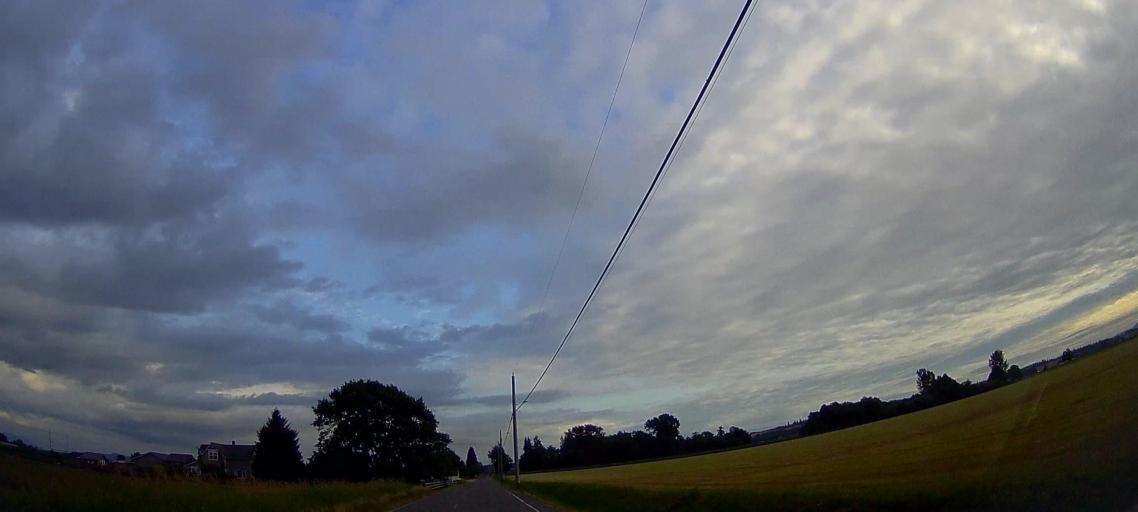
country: US
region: Washington
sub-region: Skagit County
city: Burlington
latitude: 48.5372
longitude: -122.4114
